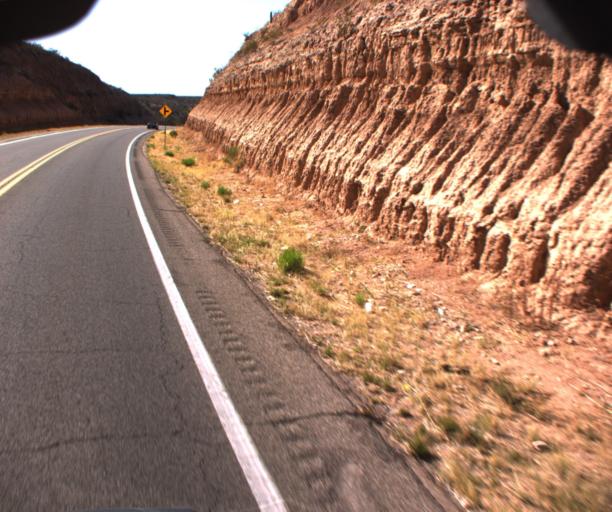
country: US
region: Arizona
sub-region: Cochise County
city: Saint David
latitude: 31.8171
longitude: -110.1673
